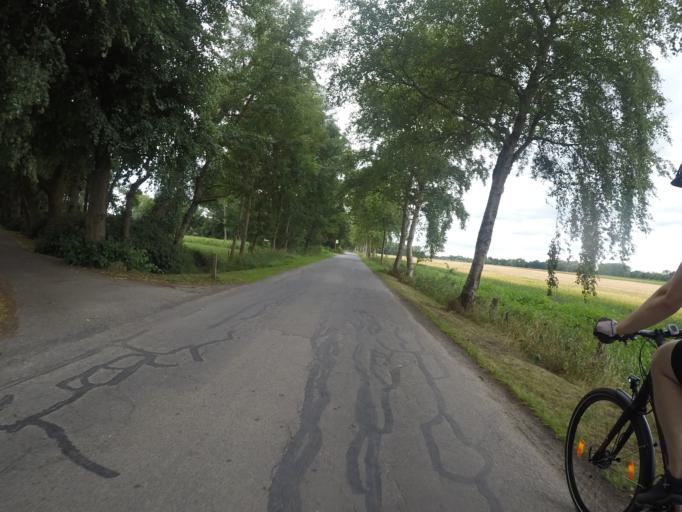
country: DE
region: Lower Saxony
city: Grossenworden
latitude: 53.6853
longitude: 9.2352
